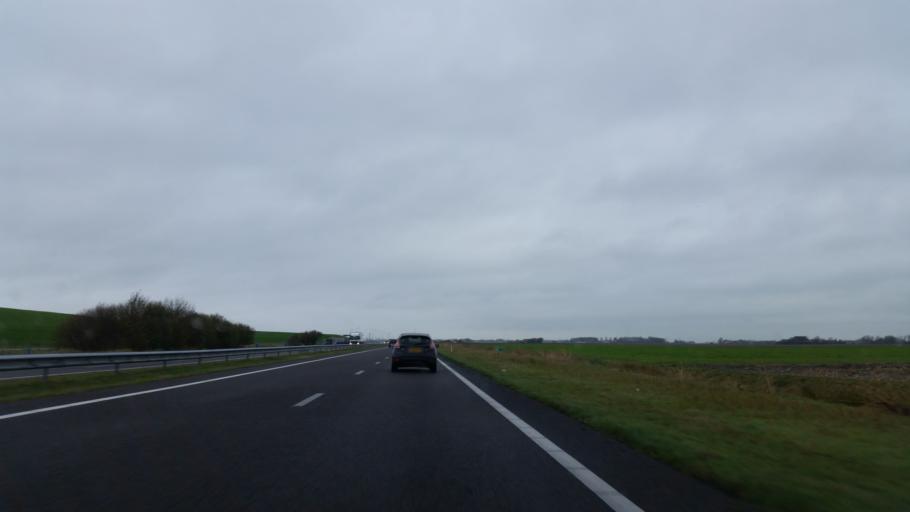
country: NL
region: Friesland
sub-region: Gemeente Harlingen
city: Harlingen
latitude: 53.1226
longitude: 5.4068
